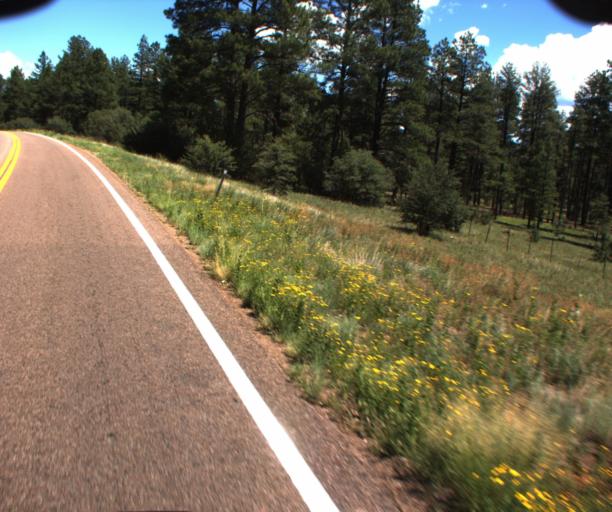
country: US
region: Arizona
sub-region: Navajo County
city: Lake of the Woods
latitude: 34.1296
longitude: -110.1090
